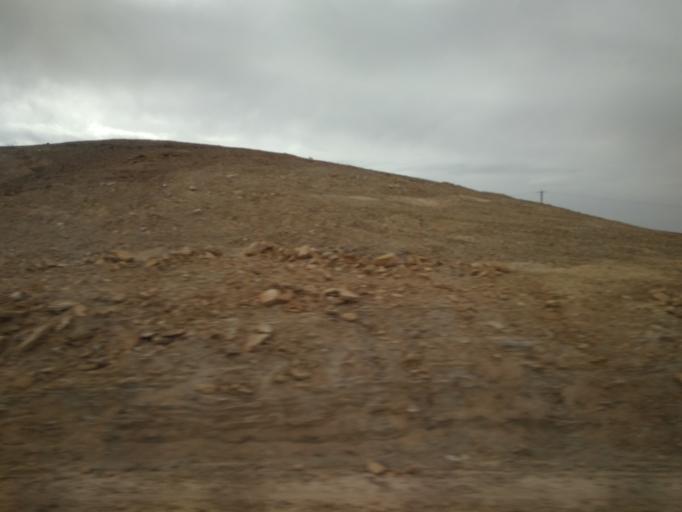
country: IL
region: Southern District
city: Eilat
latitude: 29.8896
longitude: 34.8556
